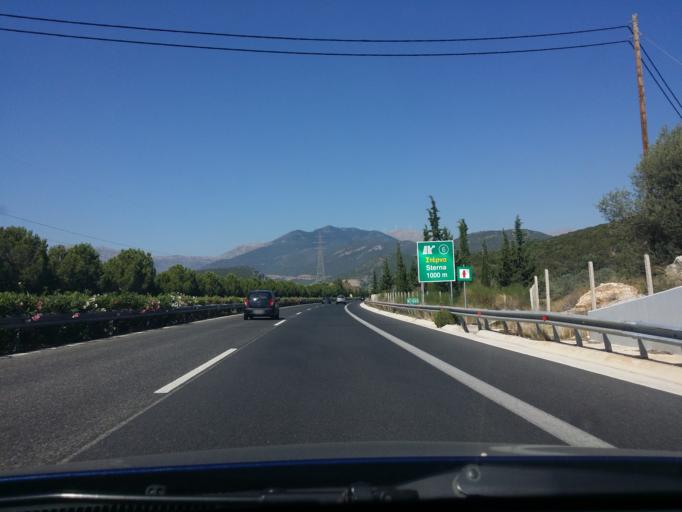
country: GR
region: Peloponnese
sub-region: Nomos Korinthias
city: Nemea
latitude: 37.7234
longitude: 22.6117
